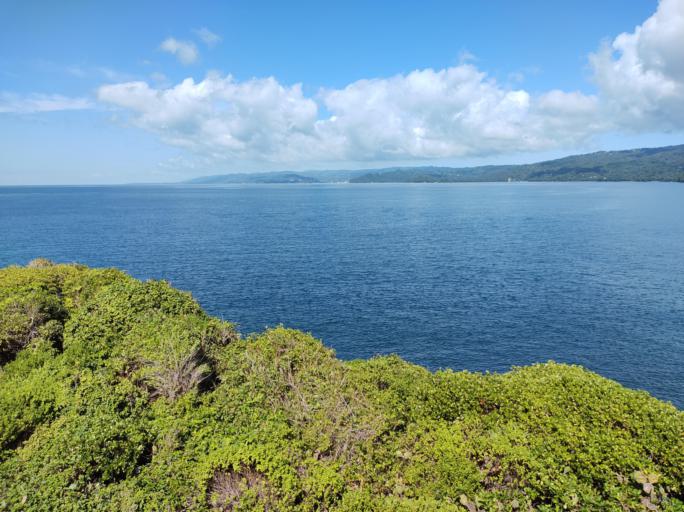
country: DO
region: Samana
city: Samana
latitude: 19.1696
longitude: -69.2703
